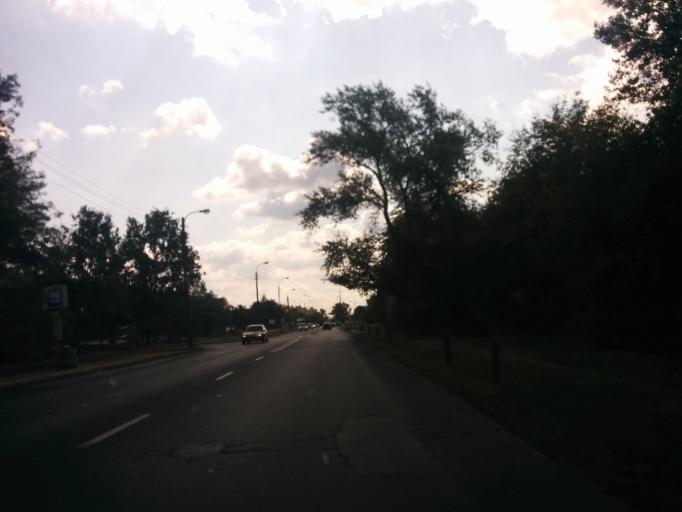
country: PL
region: Masovian Voivodeship
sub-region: Warszawa
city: Targowek
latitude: 52.3017
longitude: 21.0107
